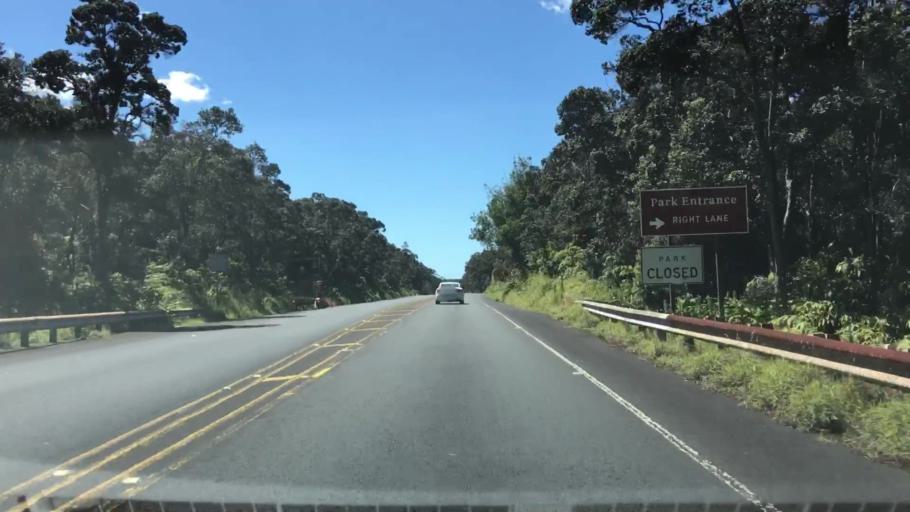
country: US
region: Hawaii
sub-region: Hawaii County
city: Volcano
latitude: 19.4310
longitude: -155.2544
